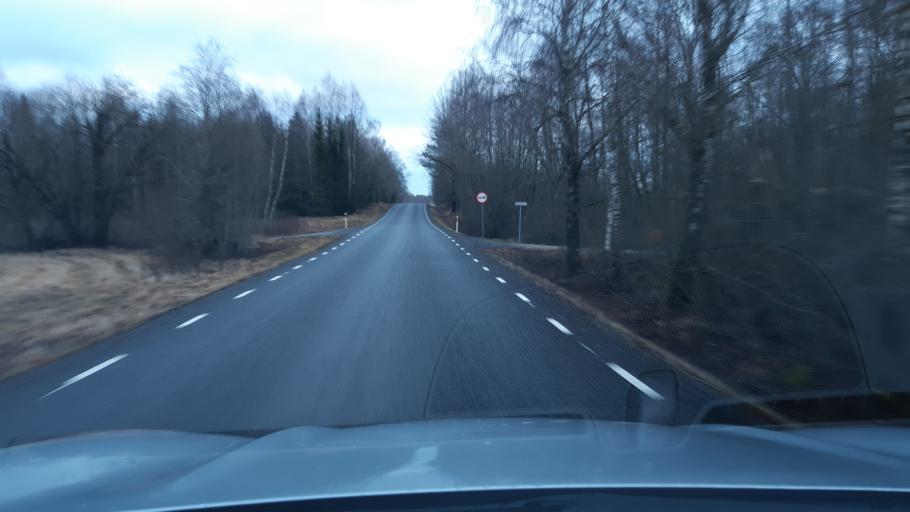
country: EE
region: Harju
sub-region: Saku vald
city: Saku
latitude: 59.2039
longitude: 24.5880
